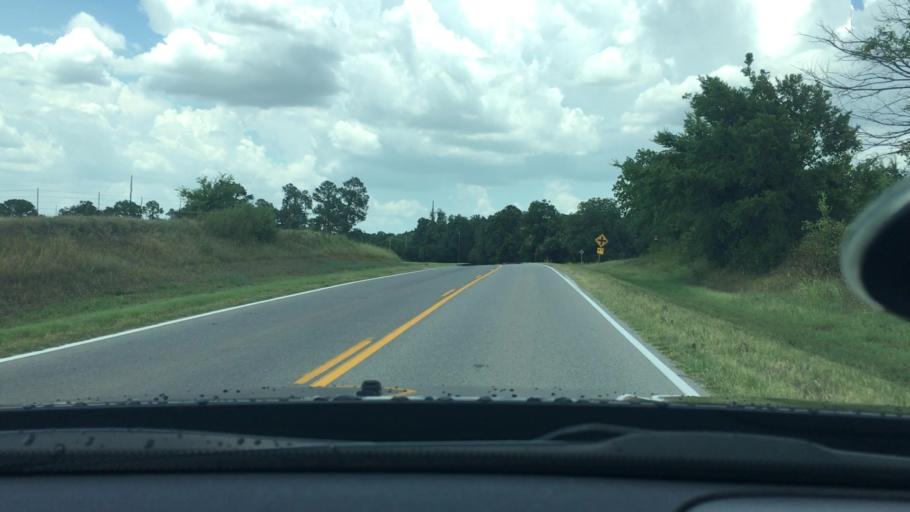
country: US
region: Oklahoma
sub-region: Johnston County
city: Tishomingo
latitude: 34.2277
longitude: -96.6979
